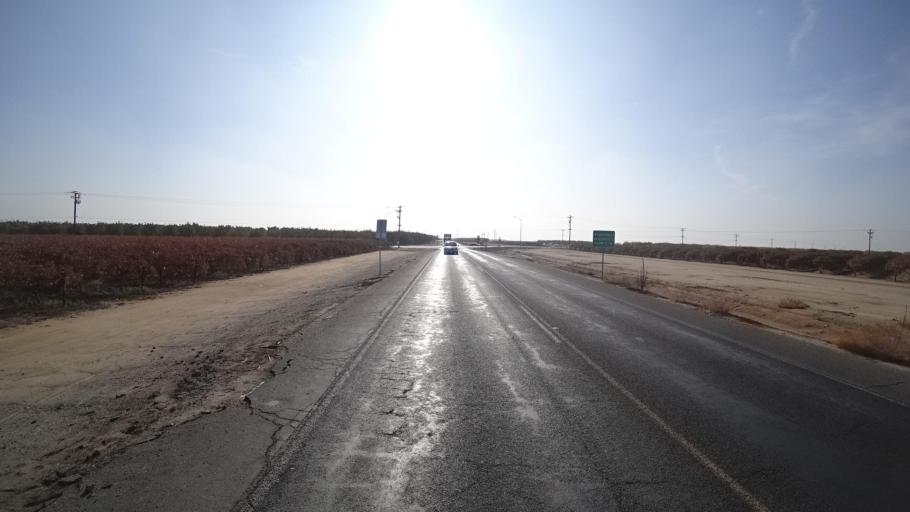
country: US
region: California
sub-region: Tulare County
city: Richgrove
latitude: 35.7624
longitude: -119.1321
